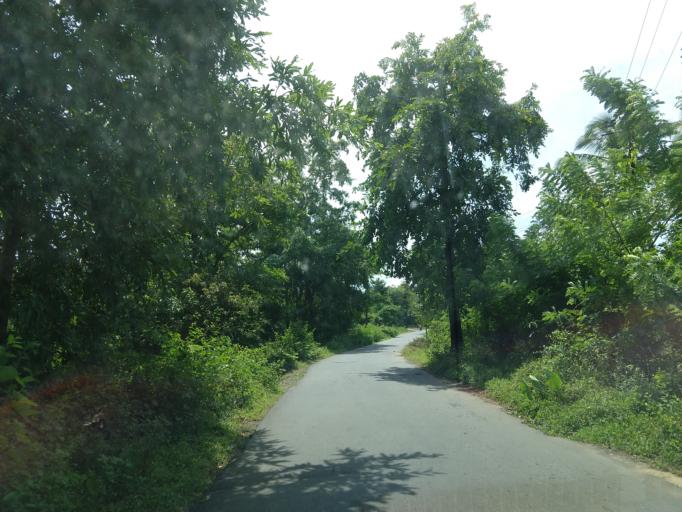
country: IN
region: Maharashtra
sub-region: Sindhudurg
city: Savantvadi
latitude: 15.9551
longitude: 73.7732
